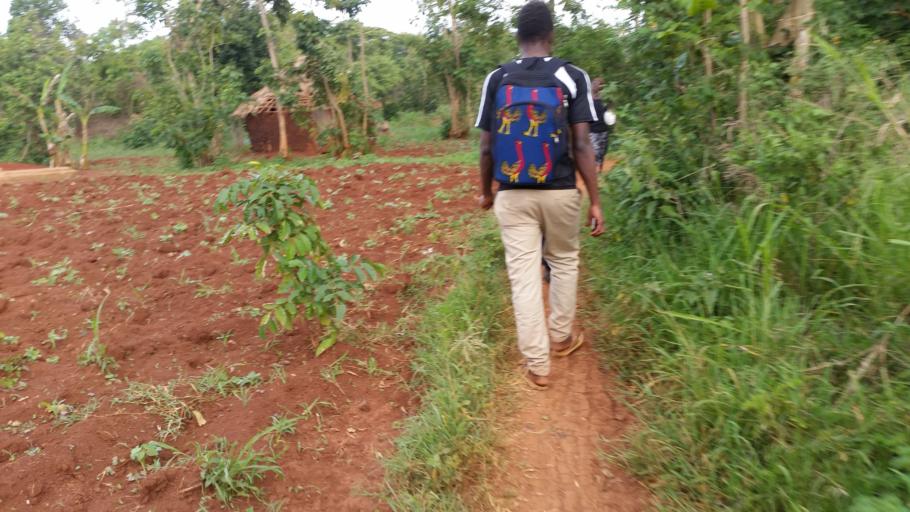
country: UG
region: Eastern Region
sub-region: Busia District
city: Busia
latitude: 0.5351
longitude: 34.0347
